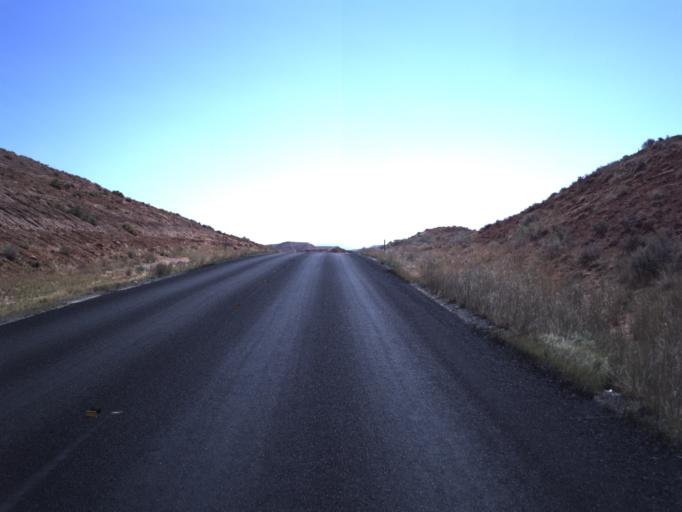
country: US
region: Utah
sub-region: Uintah County
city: Maeser
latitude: 40.4152
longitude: -109.7498
